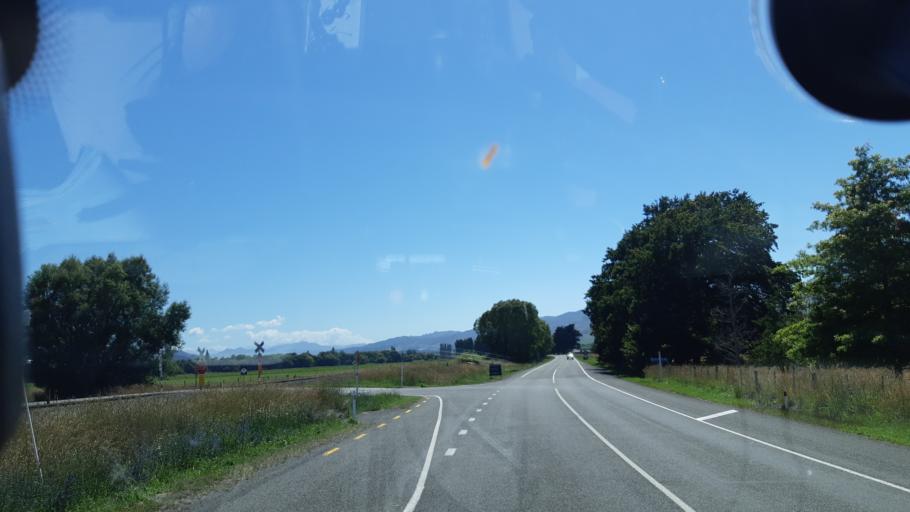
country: NZ
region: Canterbury
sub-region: Kaikoura District
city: Kaikoura
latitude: -42.7386
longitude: 173.2670
